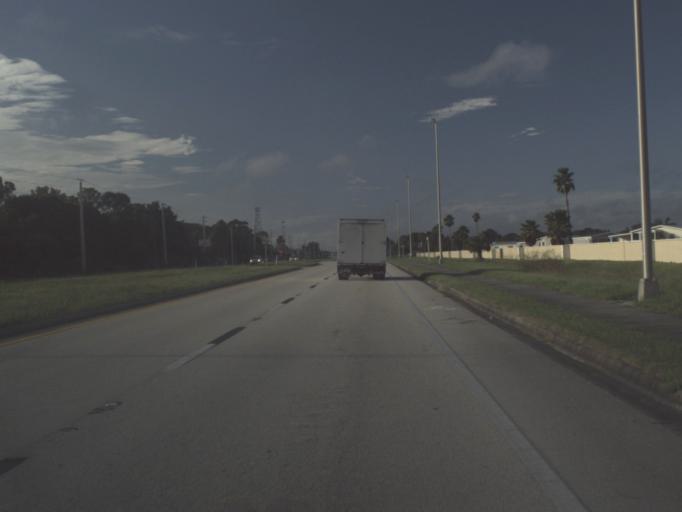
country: US
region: Florida
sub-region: Sarasota County
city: North Port
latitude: 26.9775
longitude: -82.2082
